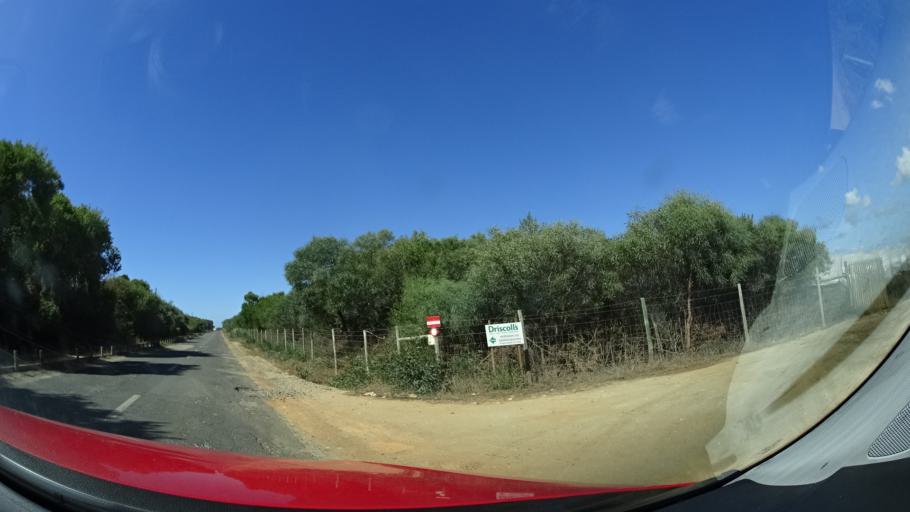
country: PT
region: Beja
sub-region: Odemira
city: Sao Teotonio
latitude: 37.5378
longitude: -8.7855
